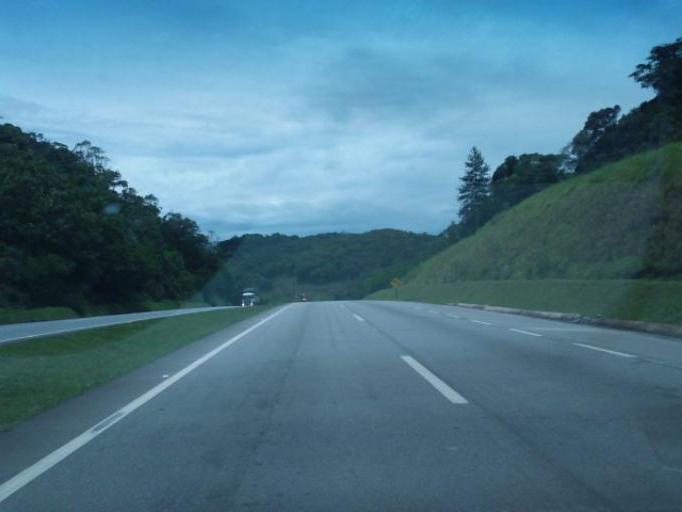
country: BR
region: Sao Paulo
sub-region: Juquitiba
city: Juquitiba
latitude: -24.0182
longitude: -47.1701
